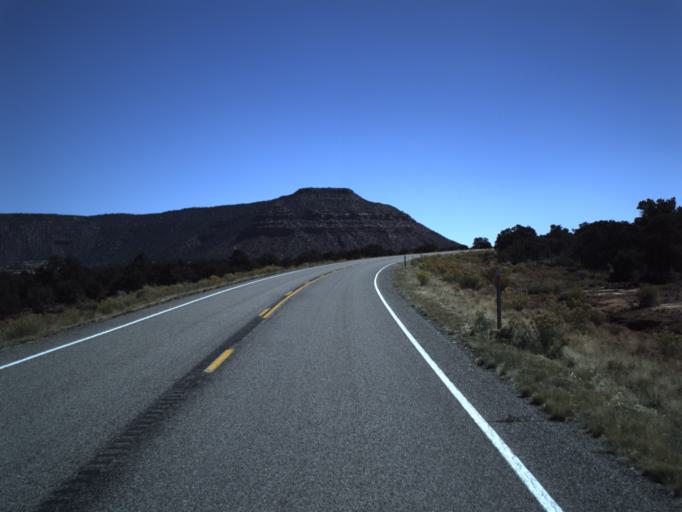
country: US
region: Utah
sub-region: San Juan County
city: Blanding
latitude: 37.6326
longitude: -110.0938
